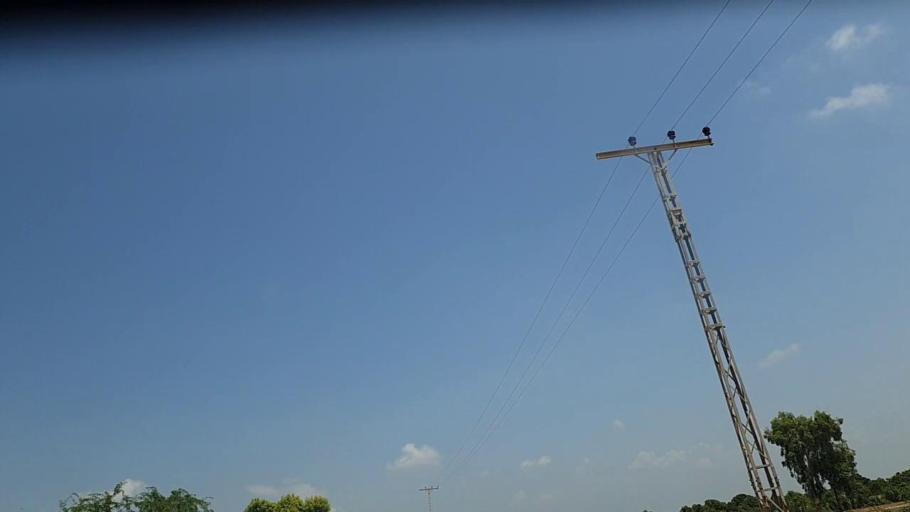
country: PK
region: Sindh
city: Bhiria
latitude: 26.9764
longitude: 68.2024
